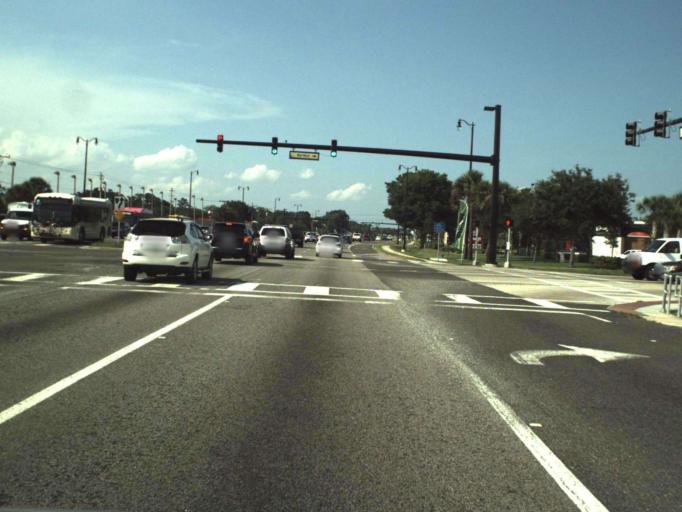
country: US
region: Florida
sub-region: Seminole County
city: Lake Mary
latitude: 28.7594
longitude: -81.2857
